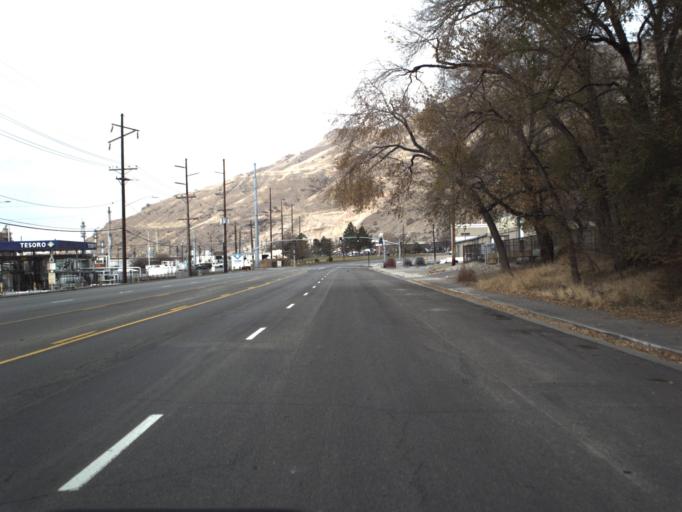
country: US
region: Utah
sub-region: Salt Lake County
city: Salt Lake City
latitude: 40.7870
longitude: -111.9025
